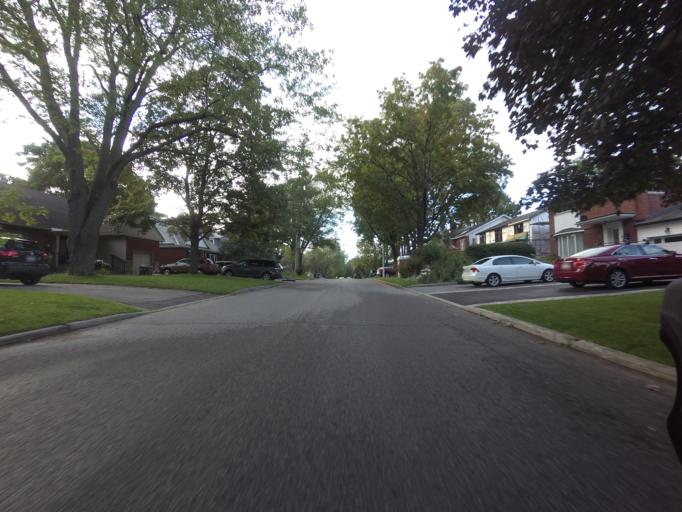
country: CA
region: Ontario
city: Ottawa
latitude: 45.3807
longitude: -75.7632
